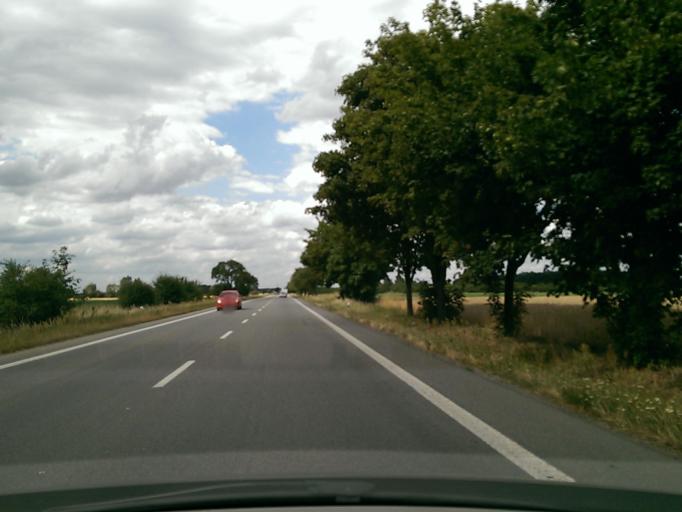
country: CZ
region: Central Bohemia
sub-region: Okres Nymburk
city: Podebrady
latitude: 50.1406
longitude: 15.0937
